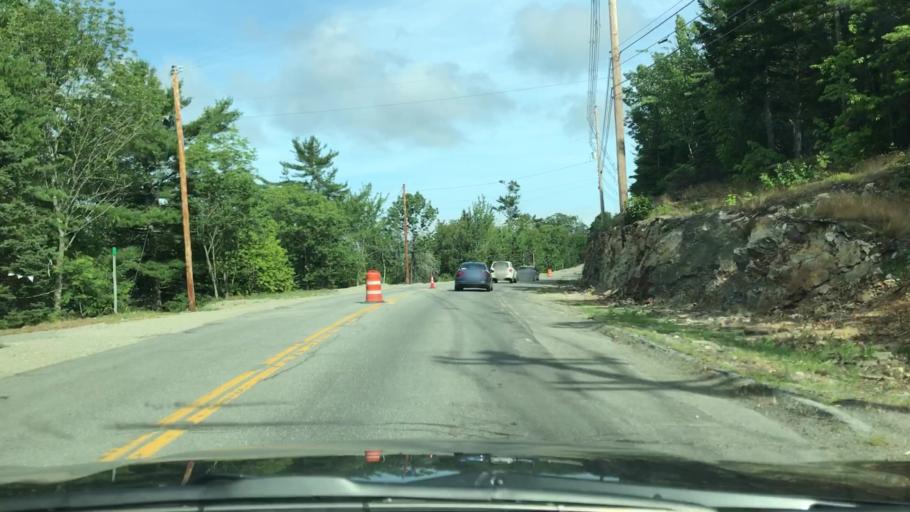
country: US
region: Maine
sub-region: Hancock County
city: Bar Harbor
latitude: 44.4088
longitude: -68.2411
